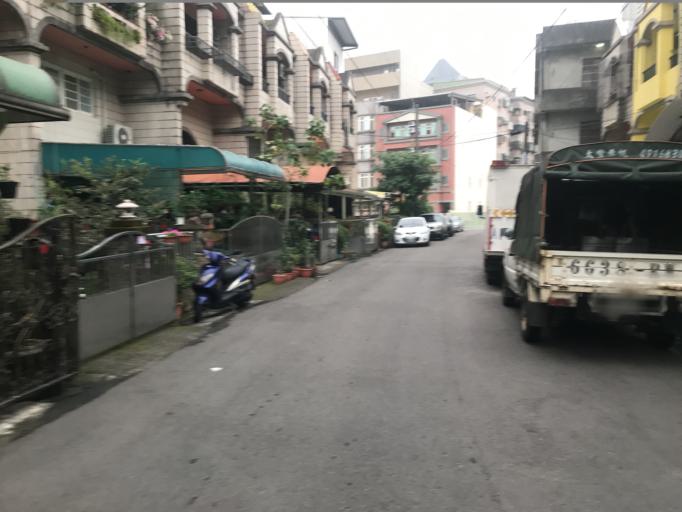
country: TW
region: Taiwan
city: Taoyuan City
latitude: 24.9529
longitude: 121.2373
